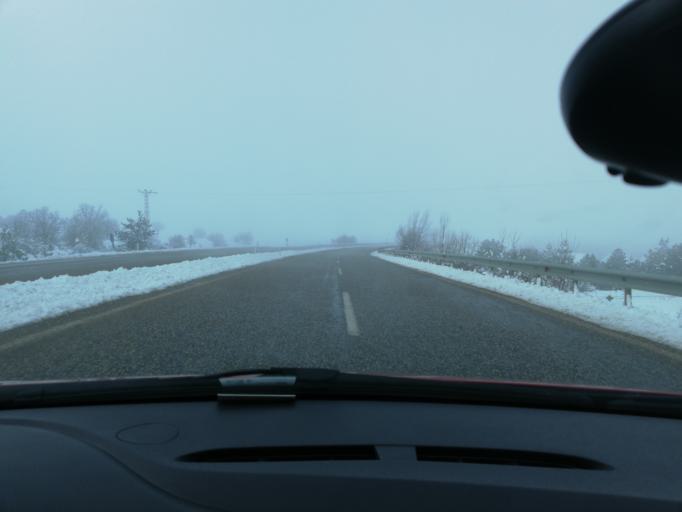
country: TR
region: Kastamonu
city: Akkaya
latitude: 41.2968
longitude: 33.5010
